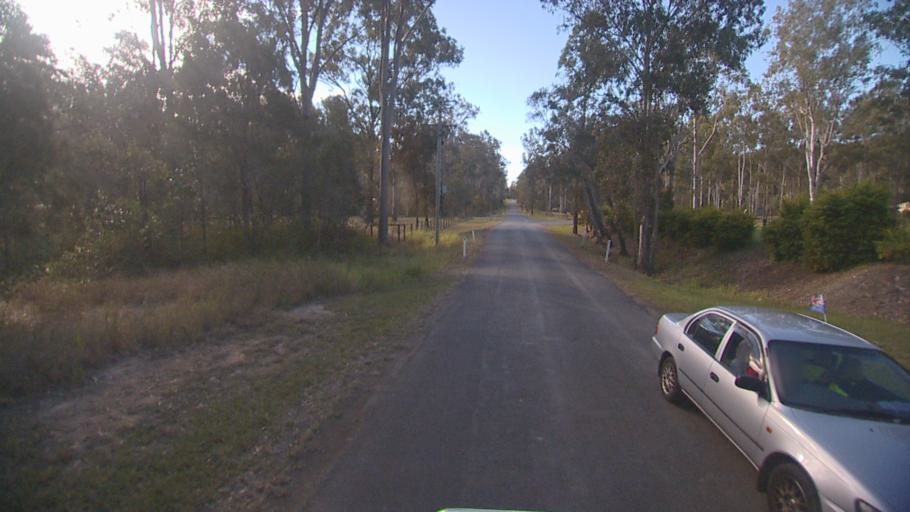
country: AU
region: Queensland
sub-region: Logan
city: Cedar Vale
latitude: -27.8255
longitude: 153.0626
